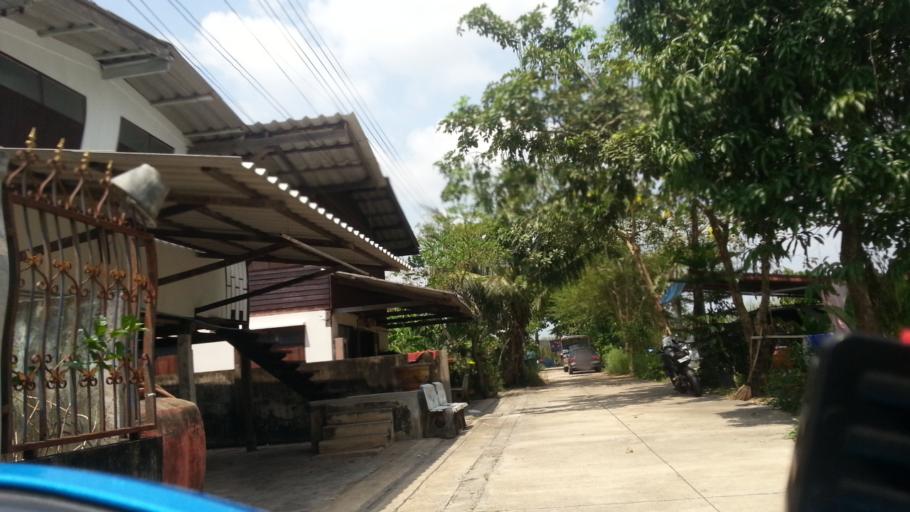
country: TH
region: Pathum Thani
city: Ban Rangsit
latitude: 14.0572
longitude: 100.8266
